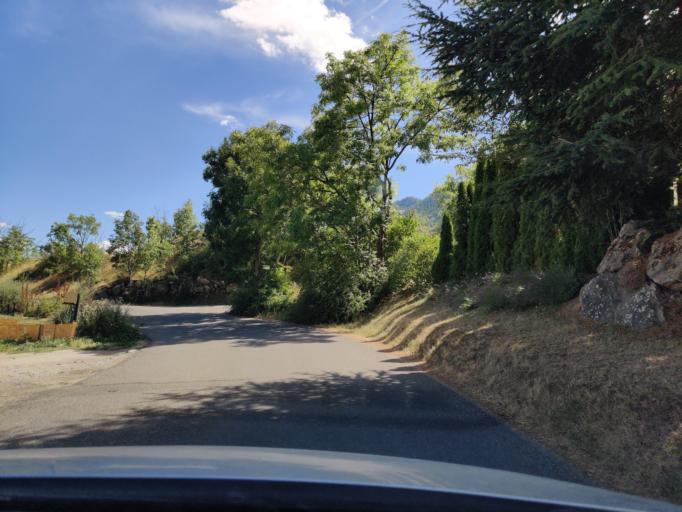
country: FR
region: Provence-Alpes-Cote d'Azur
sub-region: Departement des Hautes-Alpes
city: Saint-Martin-de-Queyrieres
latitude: 44.7392
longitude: 6.5677
